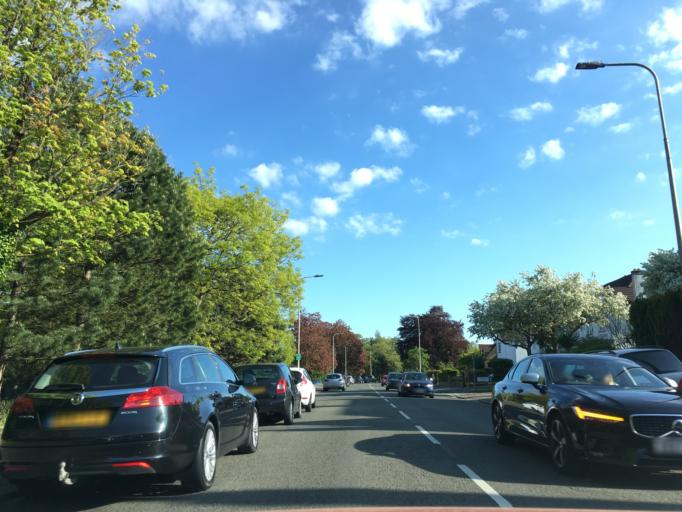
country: GB
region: Wales
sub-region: Cardiff
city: Cardiff
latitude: 51.5135
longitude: -3.1768
